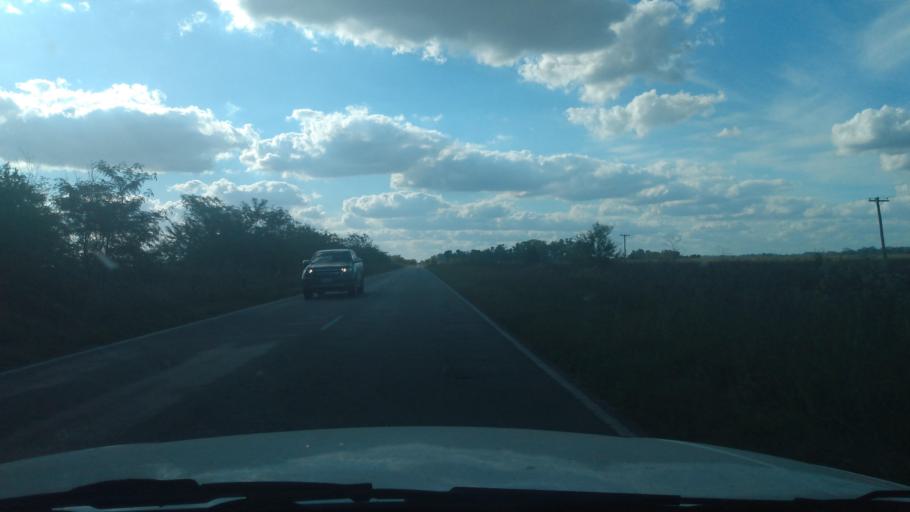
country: AR
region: Buenos Aires
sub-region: Partido de Mercedes
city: Mercedes
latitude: -34.7687
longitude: -59.3722
